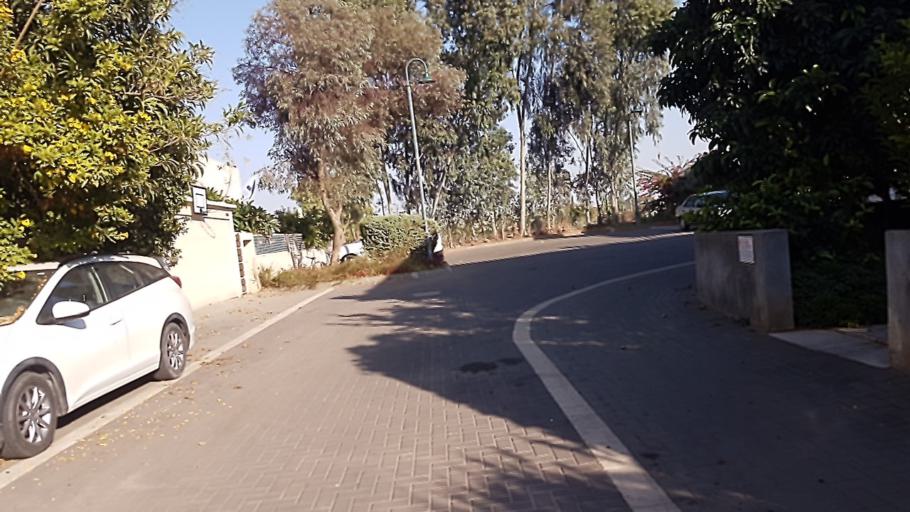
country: IL
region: Central District
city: Hod HaSharon
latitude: 32.1374
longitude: 34.9086
